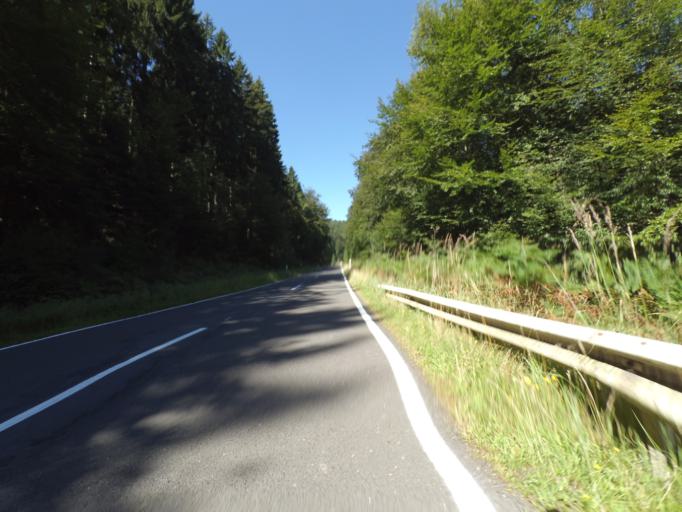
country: DE
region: Rheinland-Pfalz
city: Eisenschmitt
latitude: 50.0593
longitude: 6.7412
